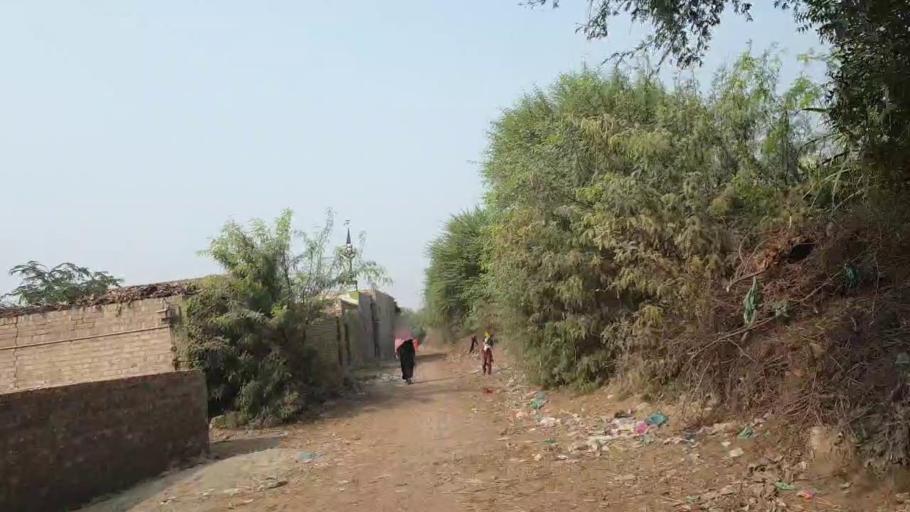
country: PK
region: Sindh
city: Tando Muhammad Khan
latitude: 25.2002
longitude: 68.5648
